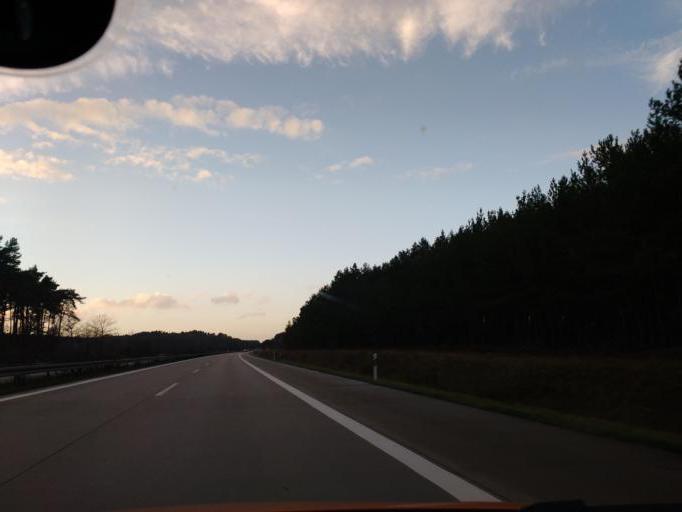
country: DE
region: Mecklenburg-Vorpommern
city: Rastow
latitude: 53.4405
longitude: 11.3816
